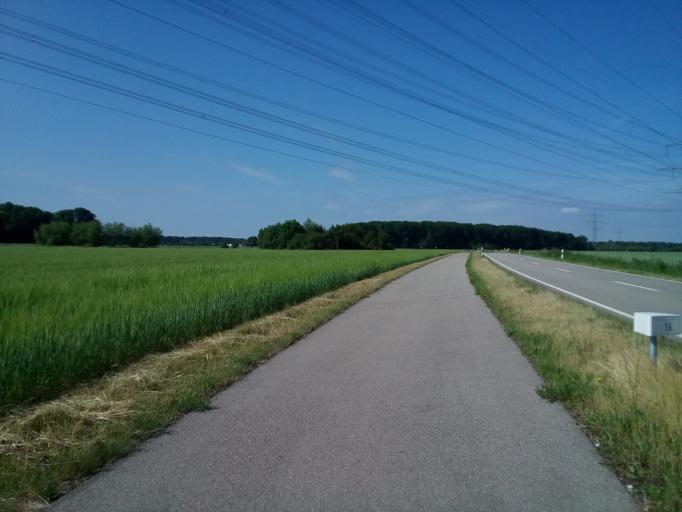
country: DE
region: Baden-Wuerttemberg
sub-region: Freiburg Region
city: Rheinau
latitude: 48.6205
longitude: 7.9171
